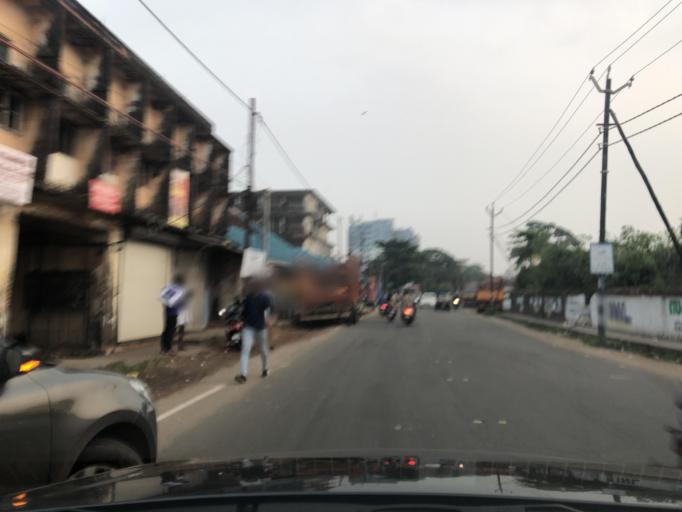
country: IN
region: Kerala
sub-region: Kozhikode
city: Kozhikode
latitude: 11.2496
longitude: 75.7725
